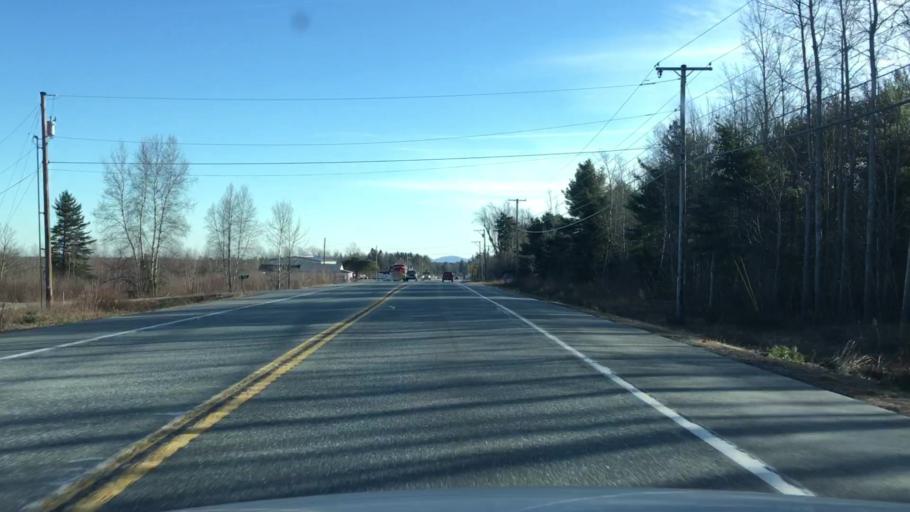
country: US
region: Maine
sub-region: Hancock County
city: Surry
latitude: 44.6189
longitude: -68.5285
